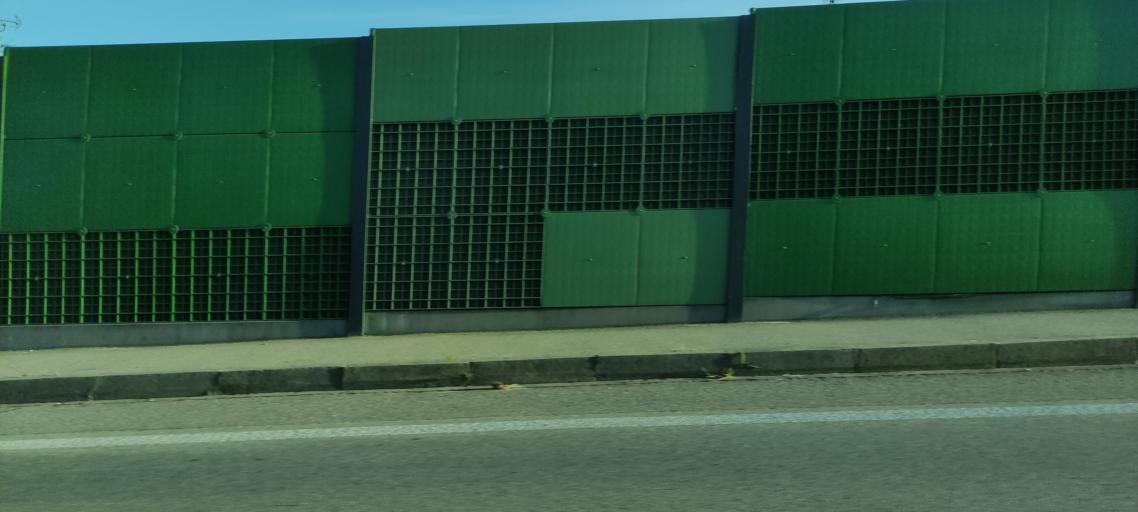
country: CZ
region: Jihocesky
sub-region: Okres Jindrichuv Hradec
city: Jindrichuv Hradec
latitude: 49.1503
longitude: 15.0163
